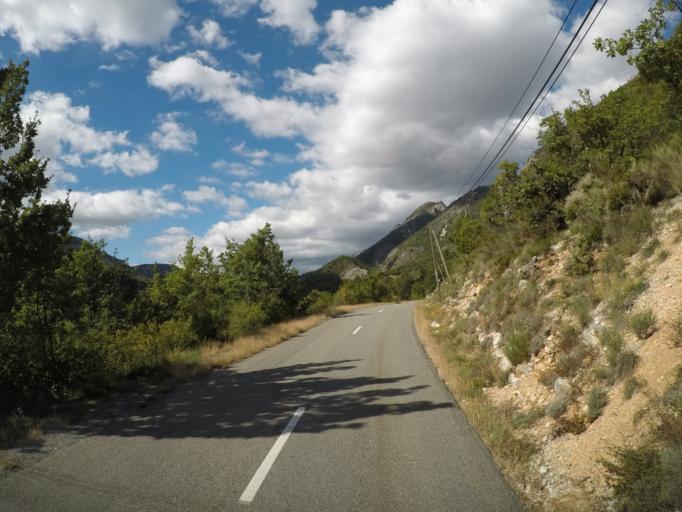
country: FR
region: Provence-Alpes-Cote d'Azur
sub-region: Departement des Hautes-Alpes
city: Laragne-Monteglin
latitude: 44.1741
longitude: 5.7171
